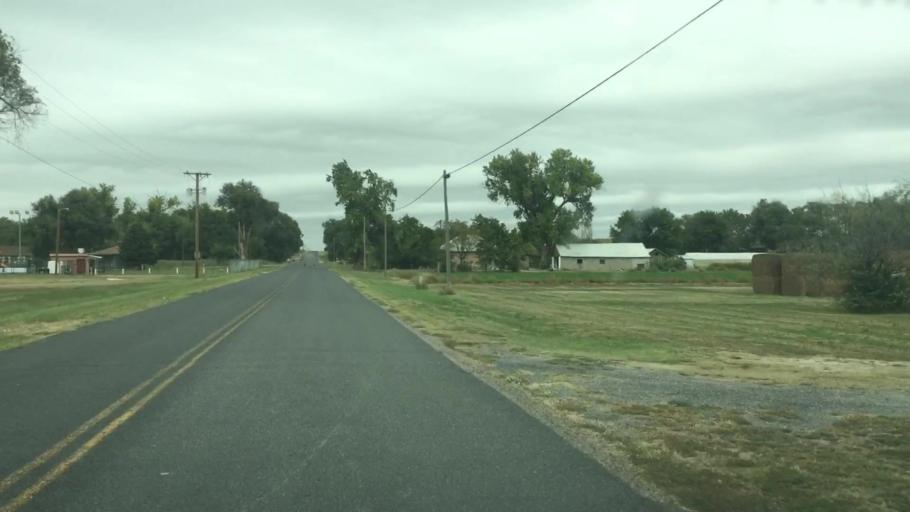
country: US
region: Kansas
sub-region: Hamilton County
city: Syracuse
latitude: 38.0554
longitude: -102.1186
